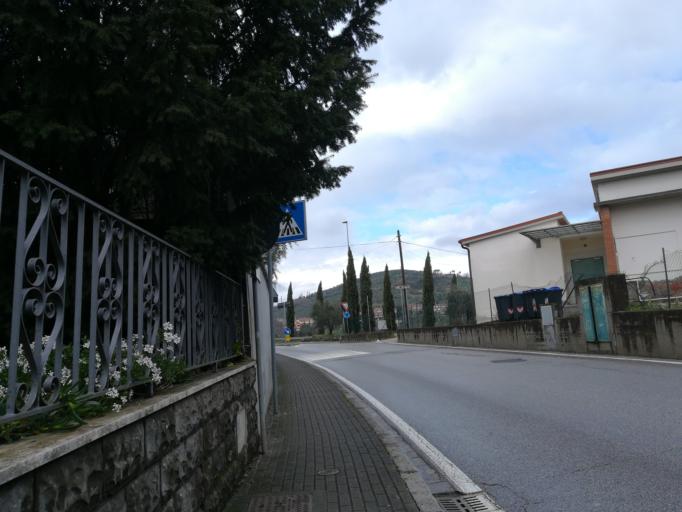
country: IT
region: Tuscany
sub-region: Provincia di Prato
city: Carmignano
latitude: 43.8039
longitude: 11.0314
